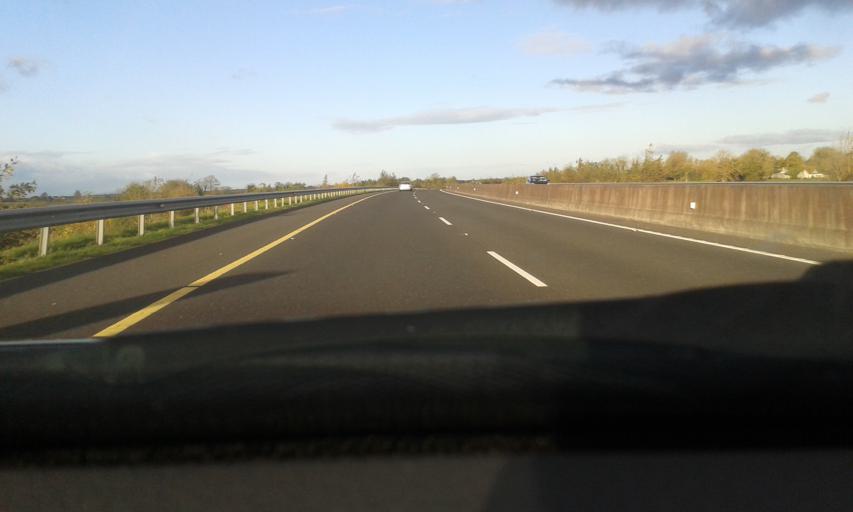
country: IE
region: Munster
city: Thurles
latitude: 52.5907
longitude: -7.8158
